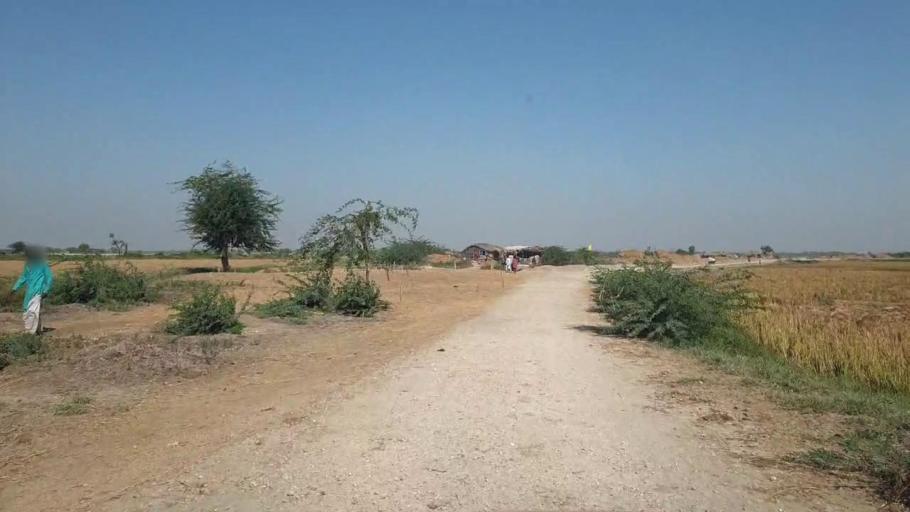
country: PK
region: Sindh
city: Talhar
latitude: 24.7813
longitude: 68.7852
